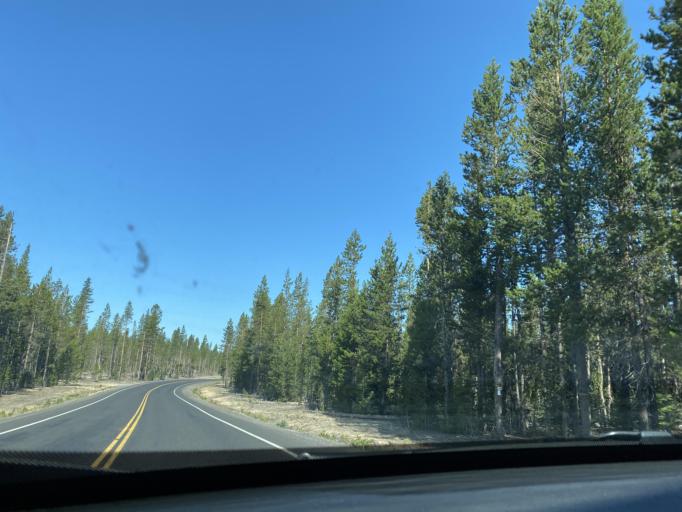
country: US
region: Oregon
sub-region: Deschutes County
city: Three Rivers
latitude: 43.7067
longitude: -121.2669
